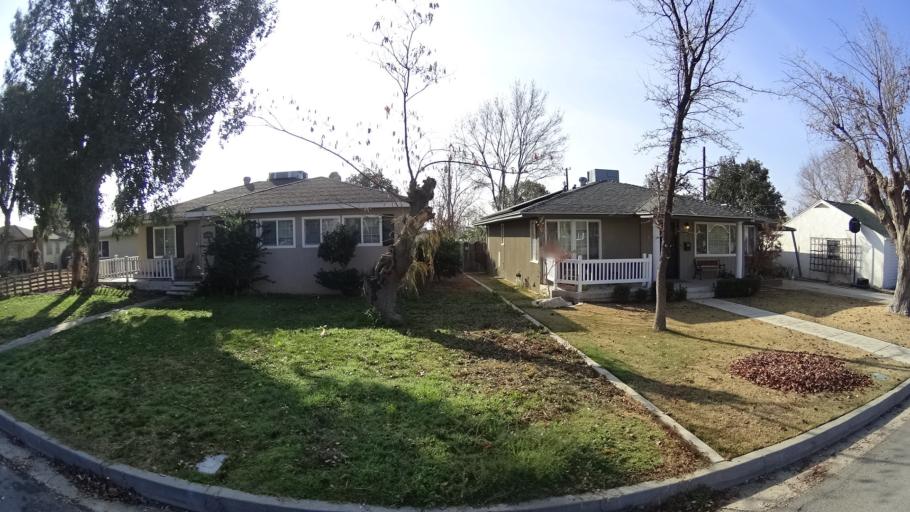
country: US
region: California
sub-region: Kern County
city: Oildale
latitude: 35.4058
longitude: -118.9908
